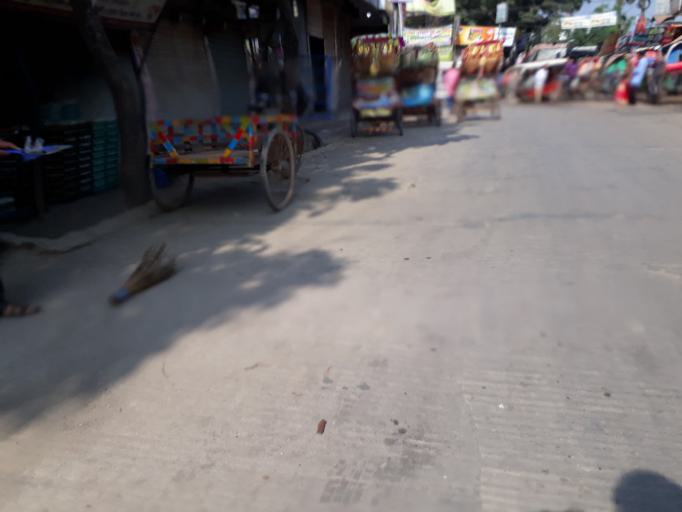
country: BD
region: Dhaka
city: Tungi
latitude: 23.8856
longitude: 90.3109
